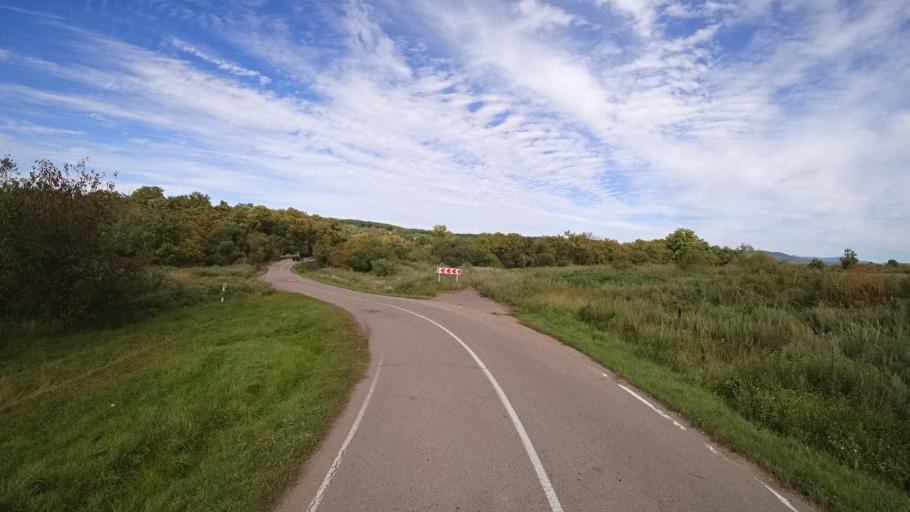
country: RU
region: Primorskiy
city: Dostoyevka
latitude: 44.3298
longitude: 133.4801
